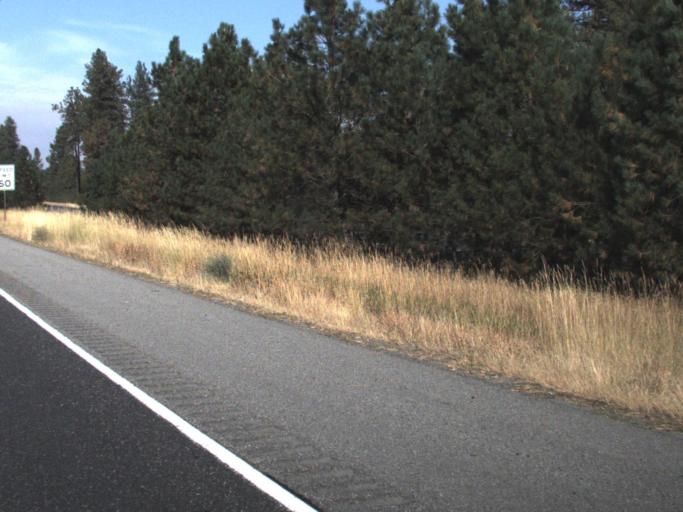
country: US
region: Washington
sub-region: Spokane County
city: Deer Park
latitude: 47.9058
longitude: -117.3508
